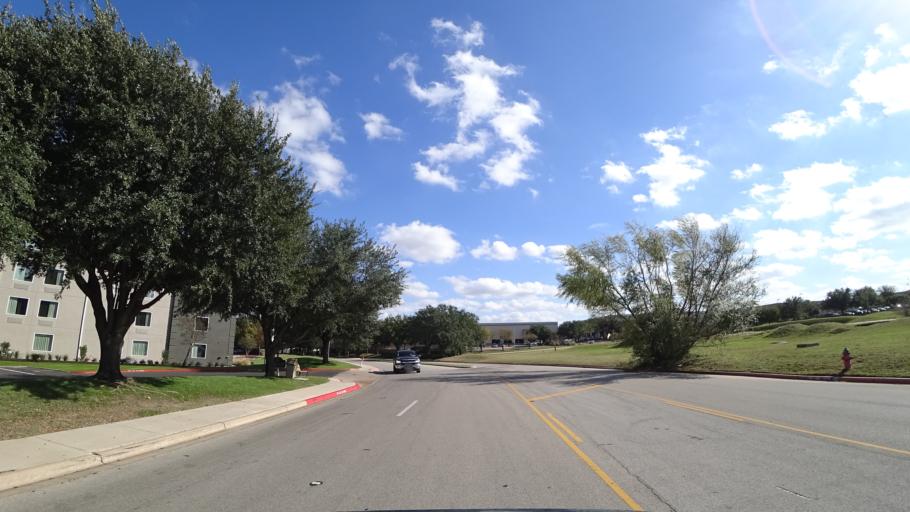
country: US
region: Texas
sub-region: Travis County
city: Wells Branch
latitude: 30.4744
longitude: -97.6747
